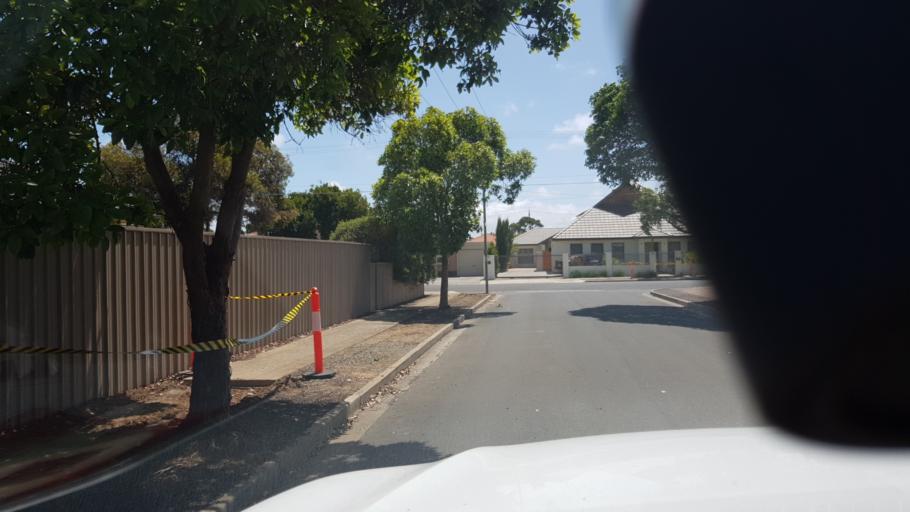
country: AU
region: South Australia
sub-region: Holdfast Bay
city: North Brighton
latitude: -35.0023
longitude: 138.5283
